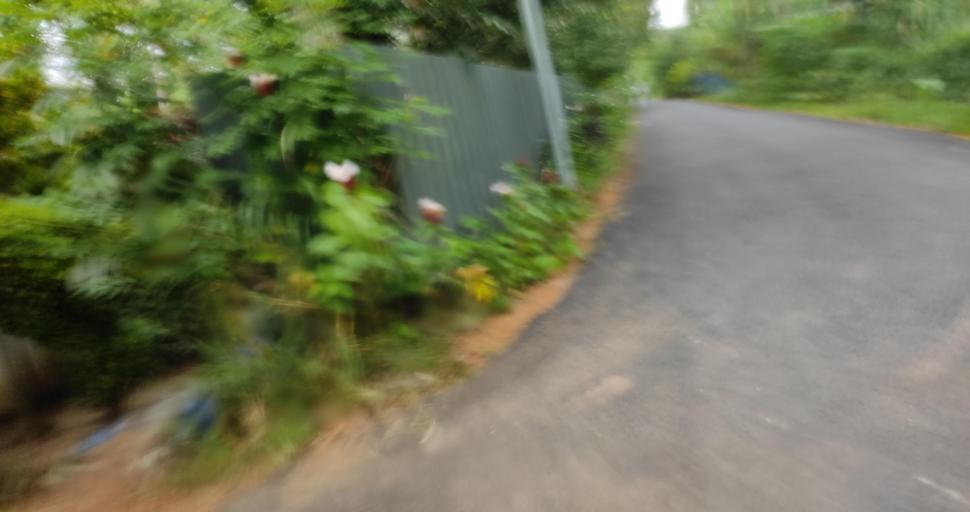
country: IN
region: Kerala
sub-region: Alappuzha
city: Shertallai
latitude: 9.6575
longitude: 76.3314
